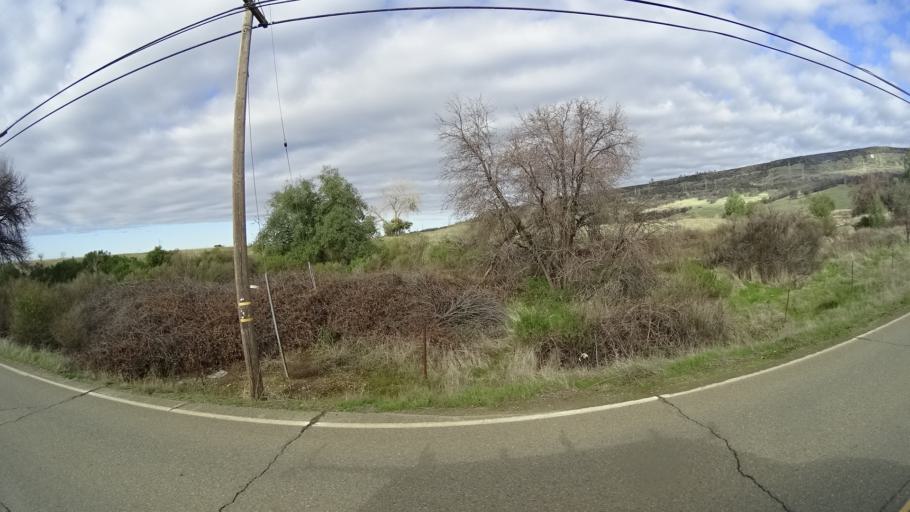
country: US
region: California
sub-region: Butte County
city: Oroville
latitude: 39.5319
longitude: -121.5534
